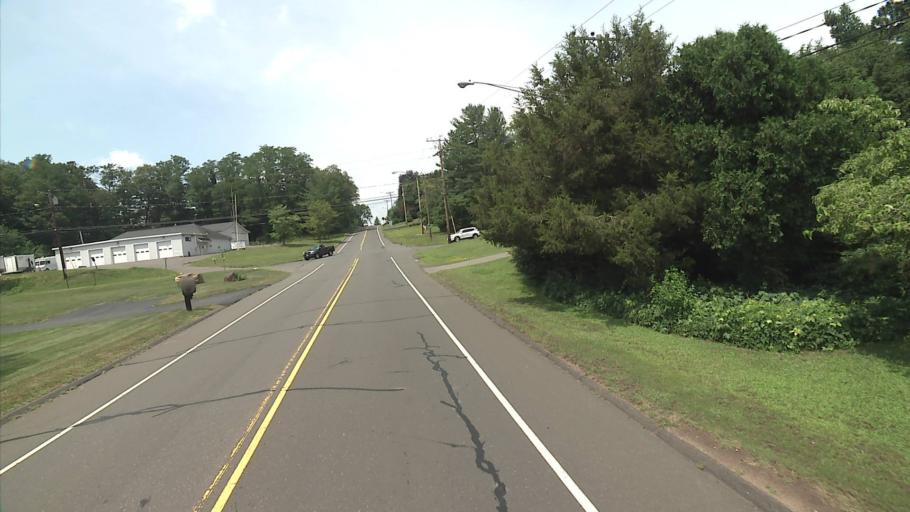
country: US
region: Connecticut
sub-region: Middlesex County
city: Middletown
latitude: 41.5332
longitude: -72.6370
